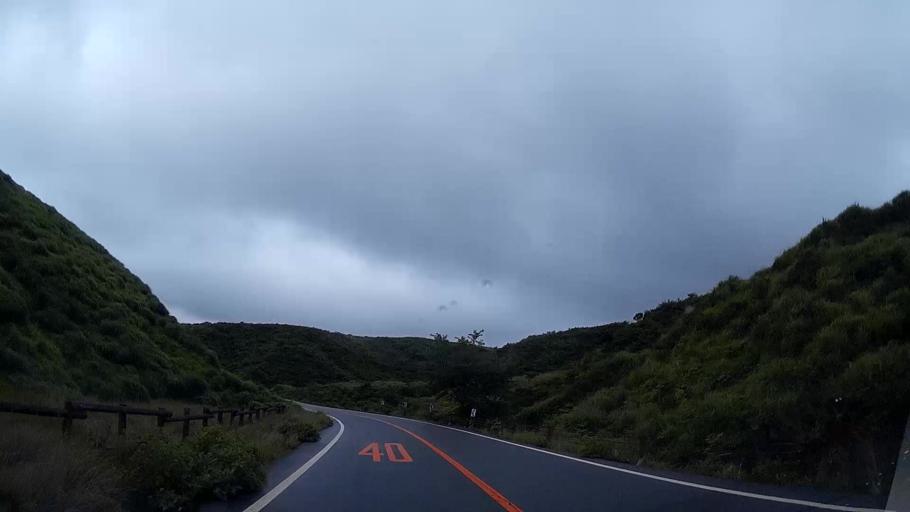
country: JP
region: Kumamoto
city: Aso
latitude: 32.8854
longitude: 131.0586
